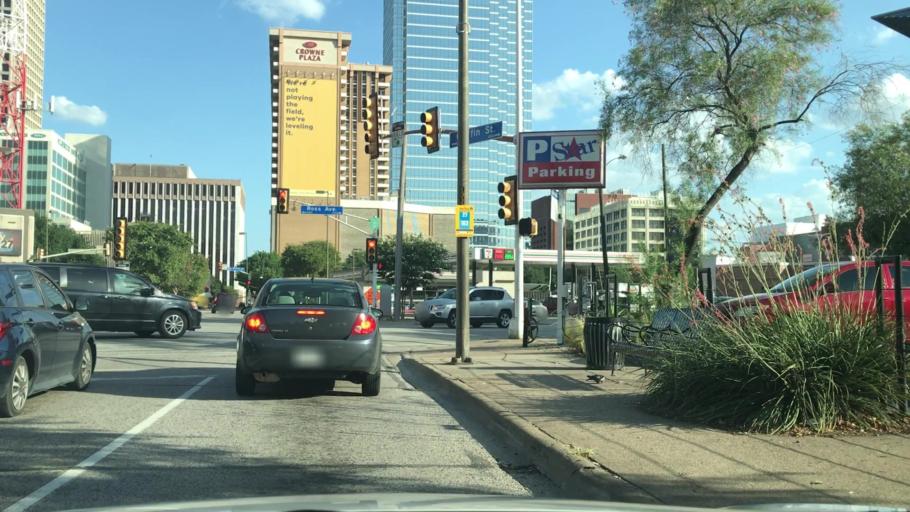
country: US
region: Texas
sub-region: Dallas County
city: Dallas
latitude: 32.7832
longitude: -96.8041
